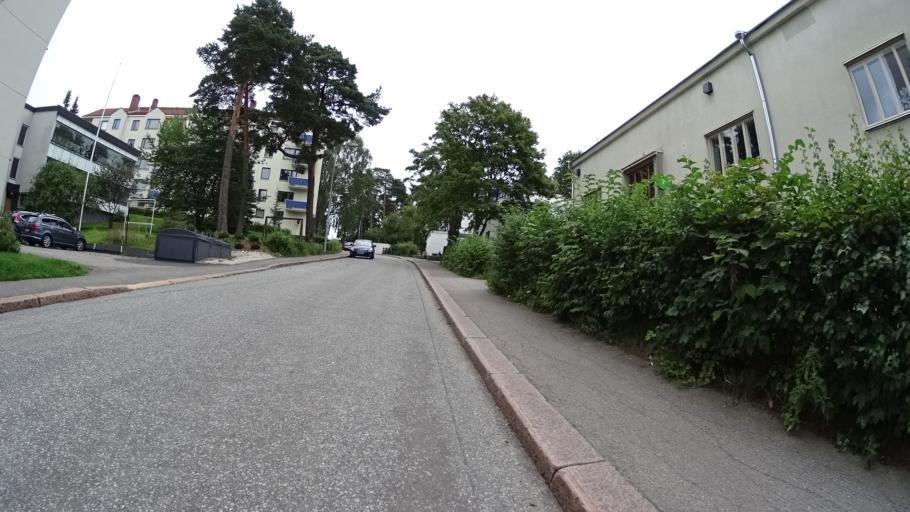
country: FI
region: Uusimaa
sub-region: Helsinki
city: Teekkarikylae
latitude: 60.1972
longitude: 24.8751
